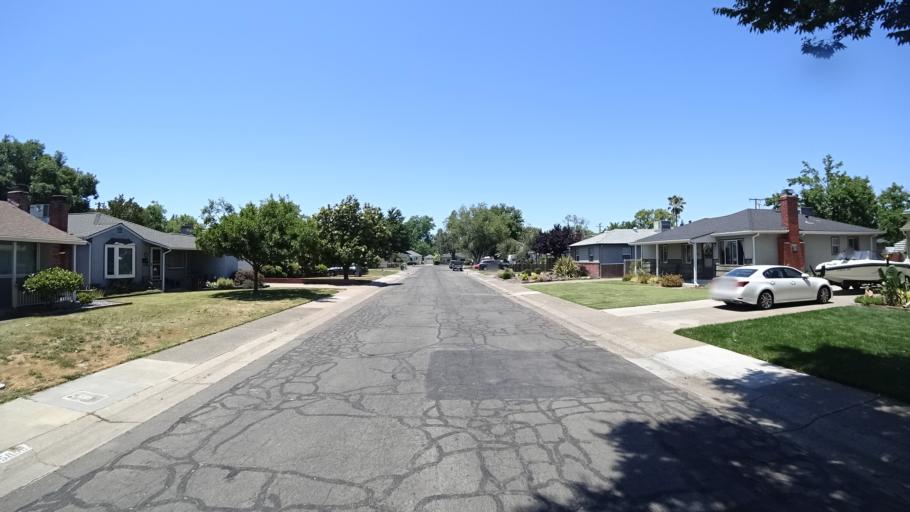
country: US
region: California
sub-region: Sacramento County
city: Parkway
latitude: 38.5358
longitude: -121.4377
